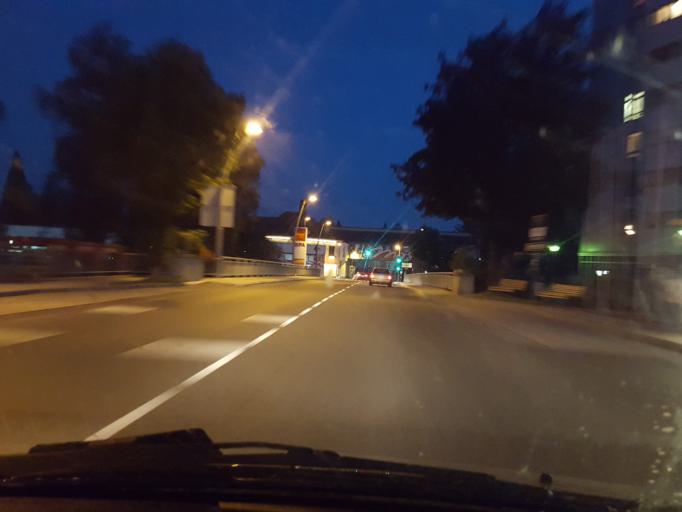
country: AT
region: Lower Austria
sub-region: Politischer Bezirk Scheibbs
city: Wieselburg
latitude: 48.1298
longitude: 15.1386
